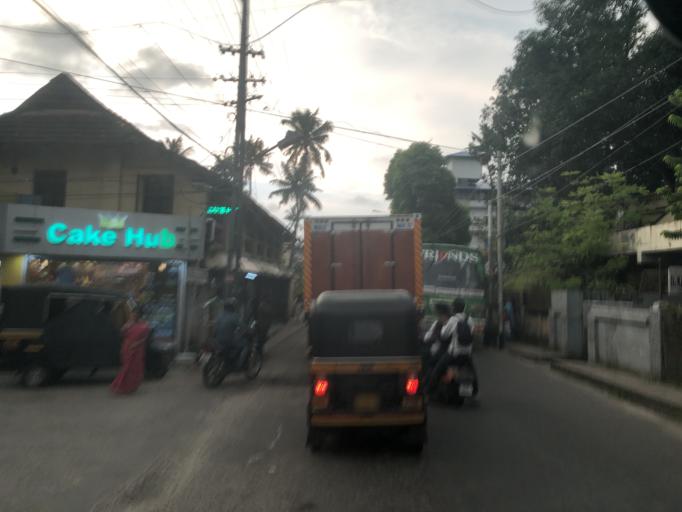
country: IN
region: Kerala
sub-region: Ernakulam
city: Cochin
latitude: 9.9521
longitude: 76.2495
